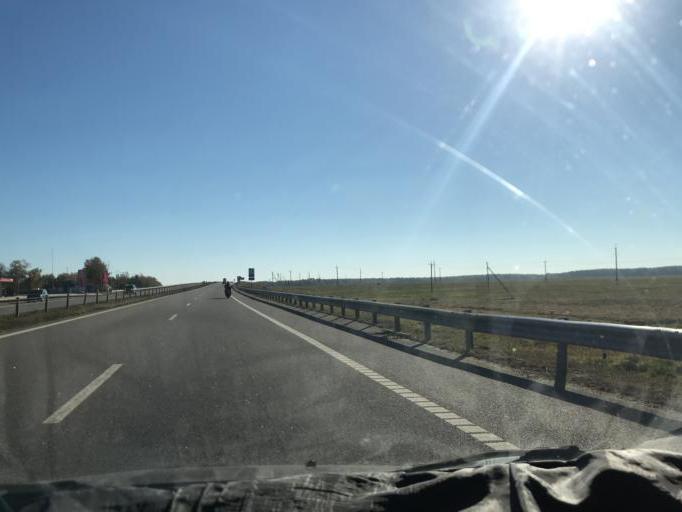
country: BY
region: Mogilev
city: Yalizava
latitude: 53.2189
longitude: 29.0282
